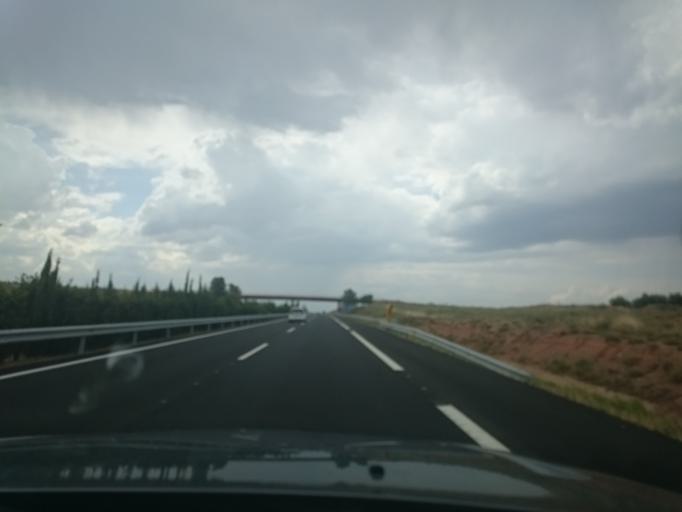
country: ES
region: La Rioja
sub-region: Provincia de La Rioja
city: Rincon de Soto
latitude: 42.2062
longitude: -1.8652
